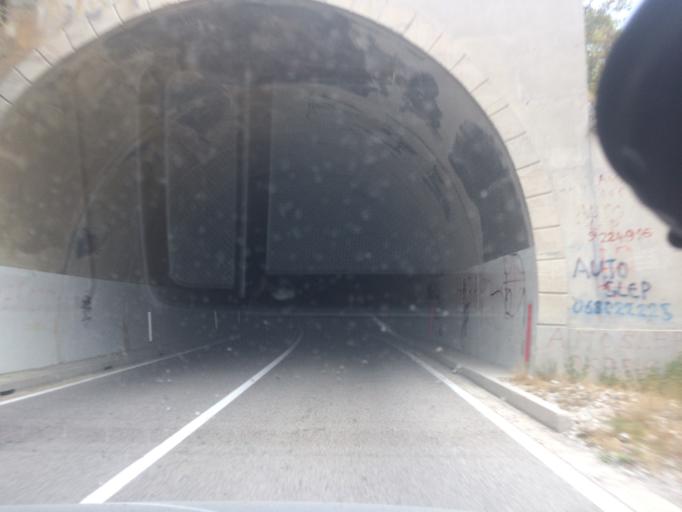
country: ME
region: Kotor
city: Risan
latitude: 42.5671
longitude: 18.6941
